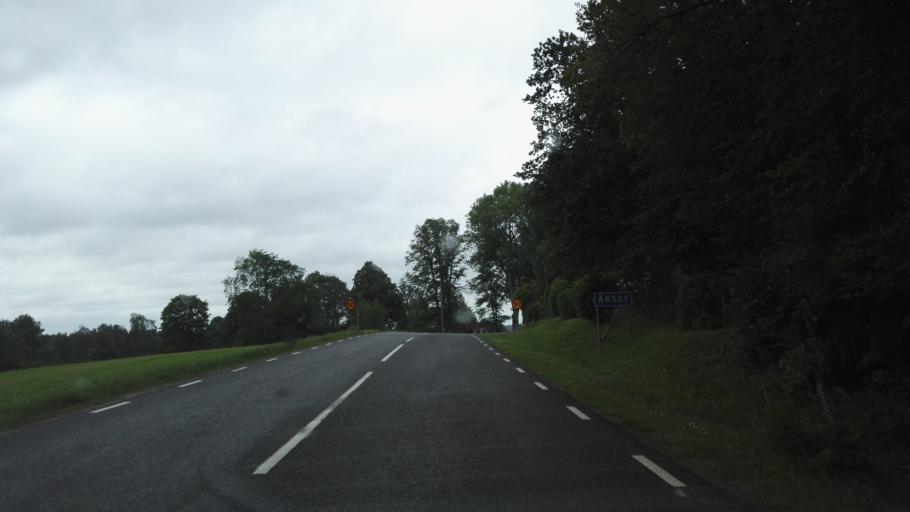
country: SE
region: Joenkoeping
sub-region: Vetlanda Kommun
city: Landsbro
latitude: 57.3109
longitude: 14.8697
